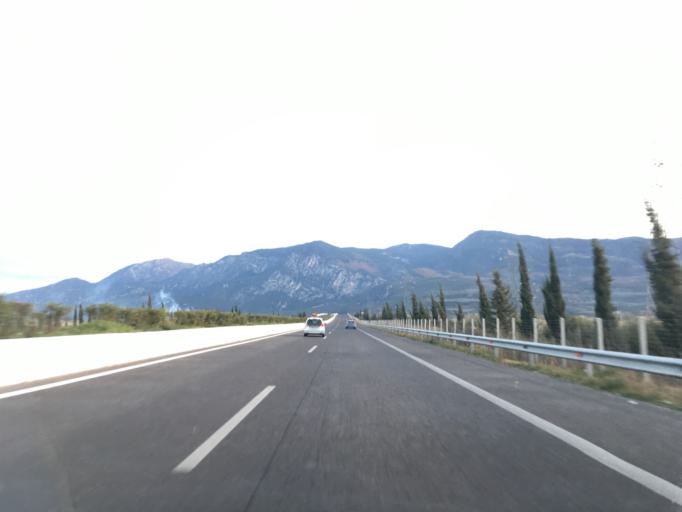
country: GR
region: Central Greece
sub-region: Nomos Fthiotidos
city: Anthili
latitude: 38.8356
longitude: 22.4795
